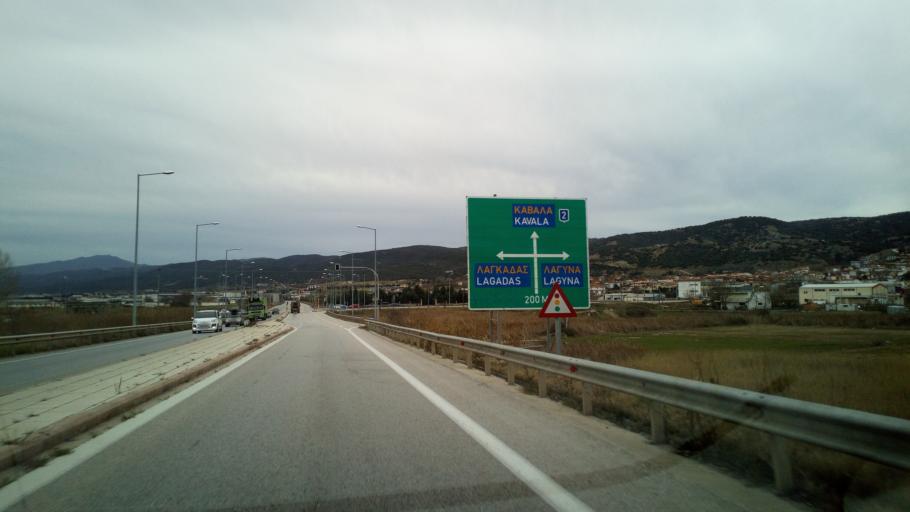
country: GR
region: Central Macedonia
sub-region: Nomos Thessalonikis
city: Lagyna
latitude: 40.7305
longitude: 23.0136
